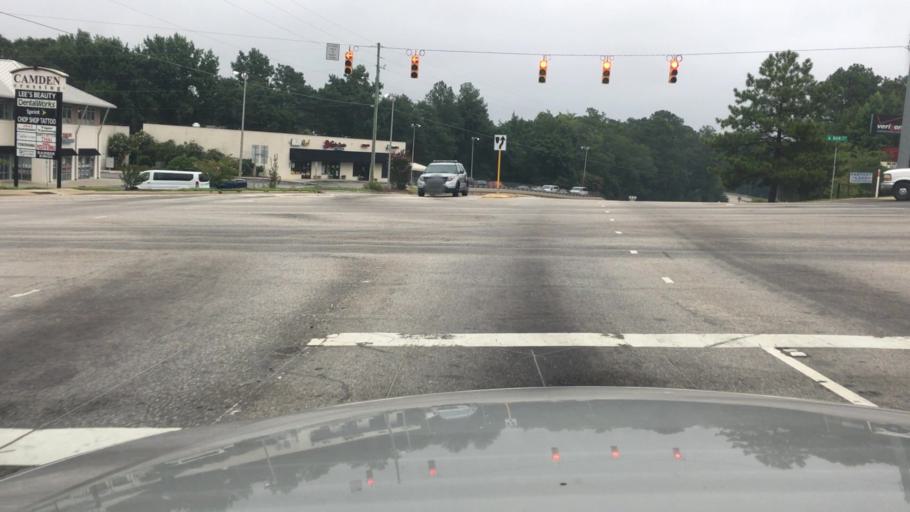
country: US
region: North Carolina
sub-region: Cumberland County
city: Hope Mills
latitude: 34.9858
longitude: -78.9652
